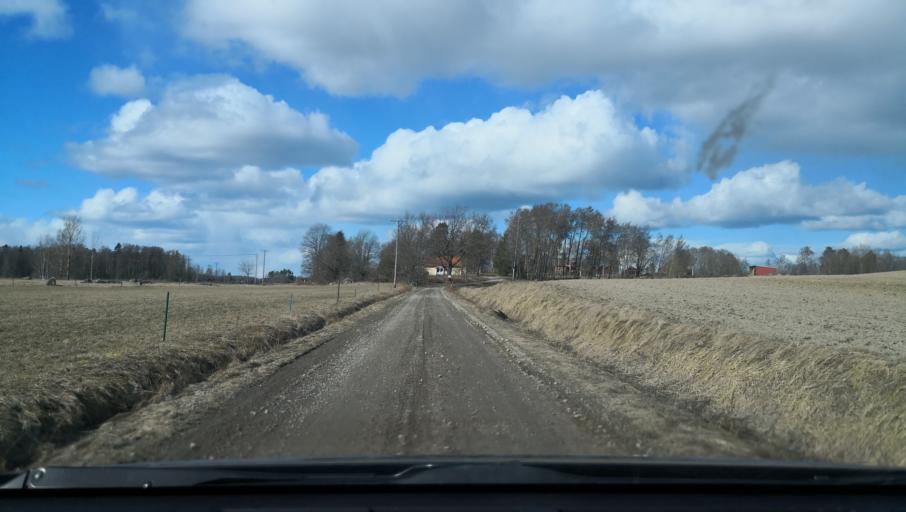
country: SE
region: OErebro
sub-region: Lindesbergs Kommun
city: Fellingsbro
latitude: 59.4149
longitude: 15.6337
